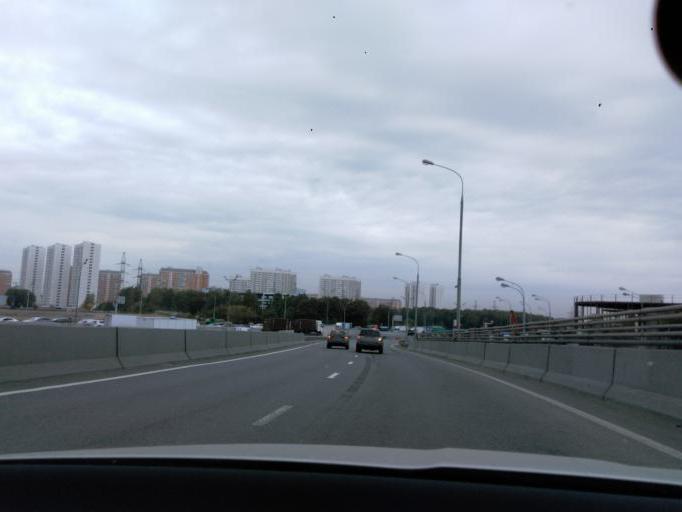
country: RU
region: Moscow
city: Vagonoremont
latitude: 55.9071
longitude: 37.5455
